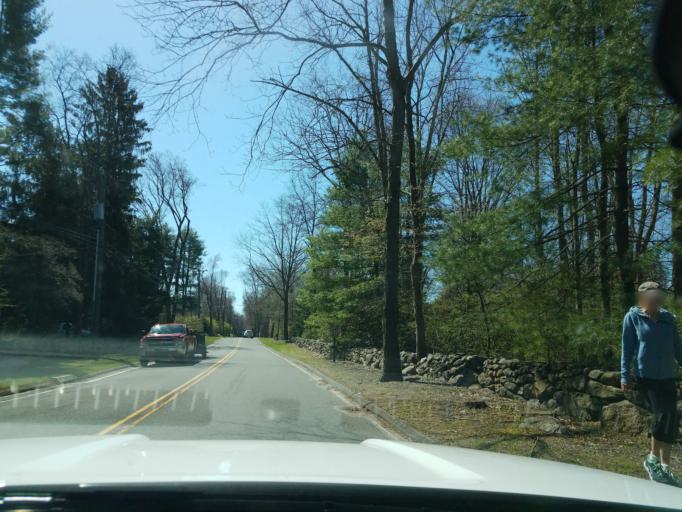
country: US
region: Connecticut
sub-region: Fairfield County
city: Wilton
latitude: 41.2184
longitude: -73.3788
